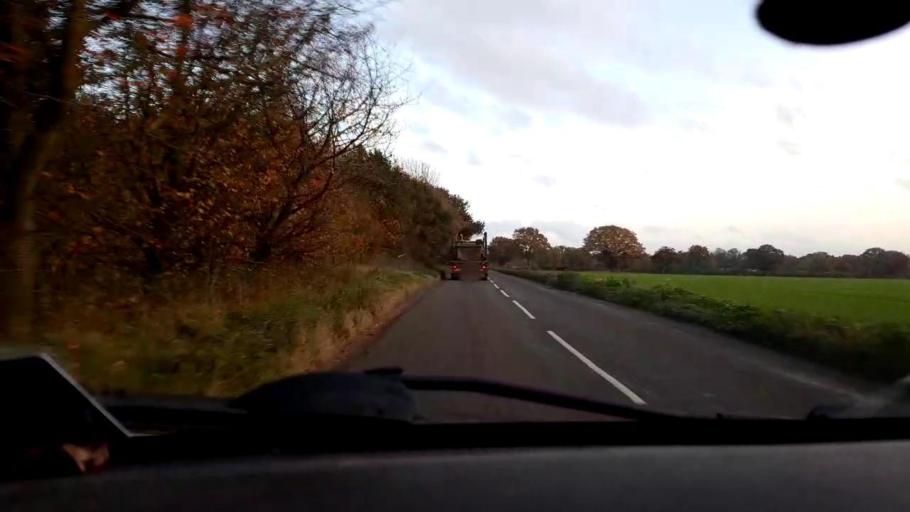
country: GB
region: England
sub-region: Norfolk
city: Mattishall
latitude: 52.6917
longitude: 1.0978
